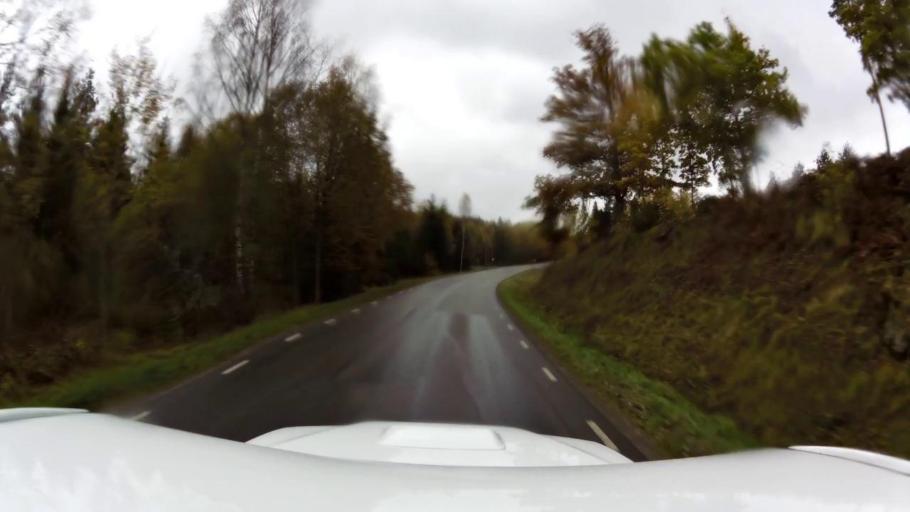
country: SE
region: OEstergoetland
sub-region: Linkopings Kommun
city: Ljungsbro
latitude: 58.5210
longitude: 15.5241
